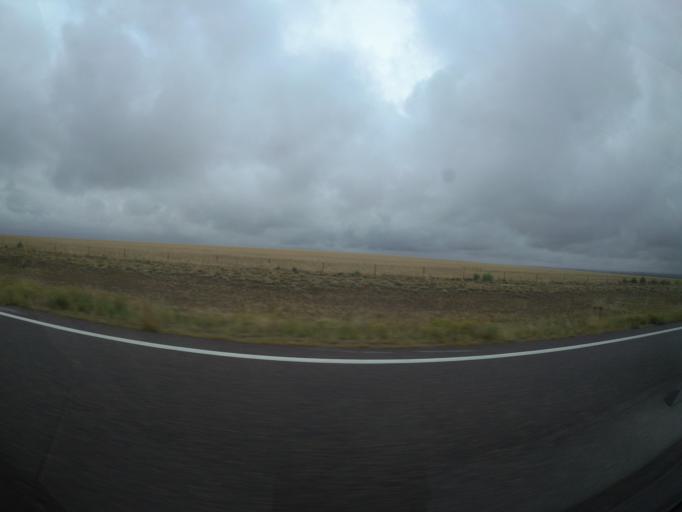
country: US
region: Colorado
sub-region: Arapahoe County
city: Byers
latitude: 39.7399
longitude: -104.0713
